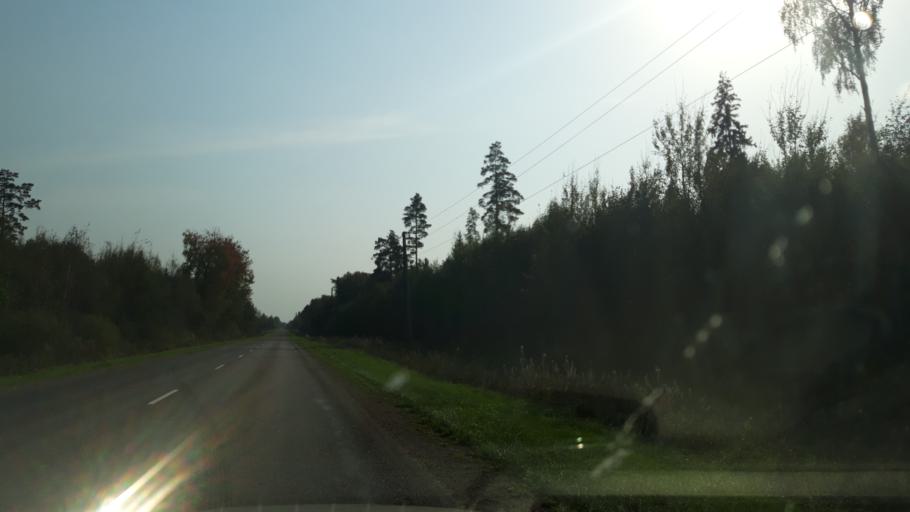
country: LV
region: Burtnieki
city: Matisi
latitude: 57.6448
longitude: 25.2442
